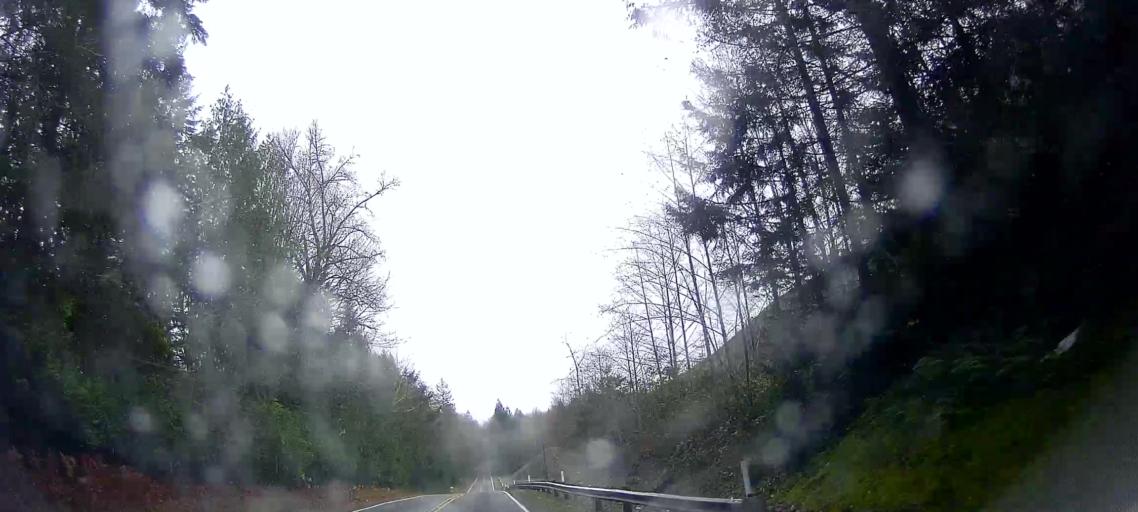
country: US
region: Washington
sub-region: Snohomish County
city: Darrington
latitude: 48.5316
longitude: -121.7982
